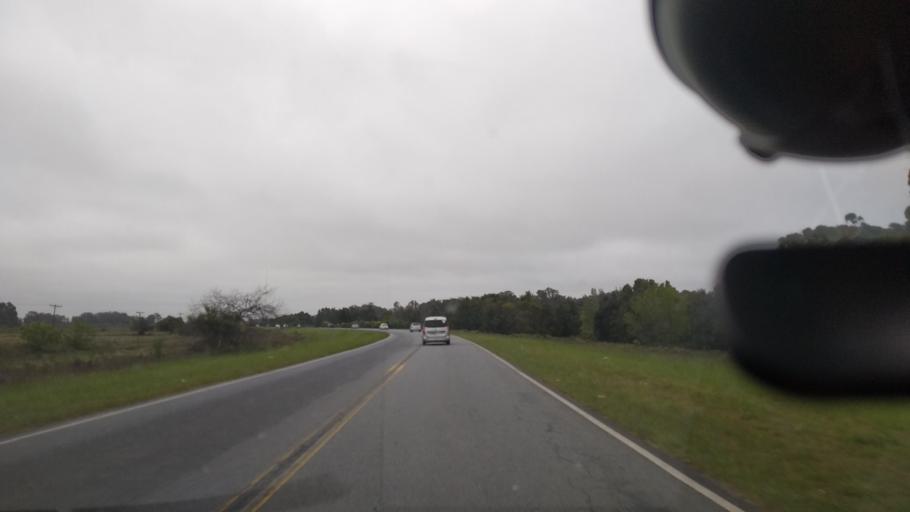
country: AR
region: Buenos Aires
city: Veronica
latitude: -35.4115
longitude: -57.3467
